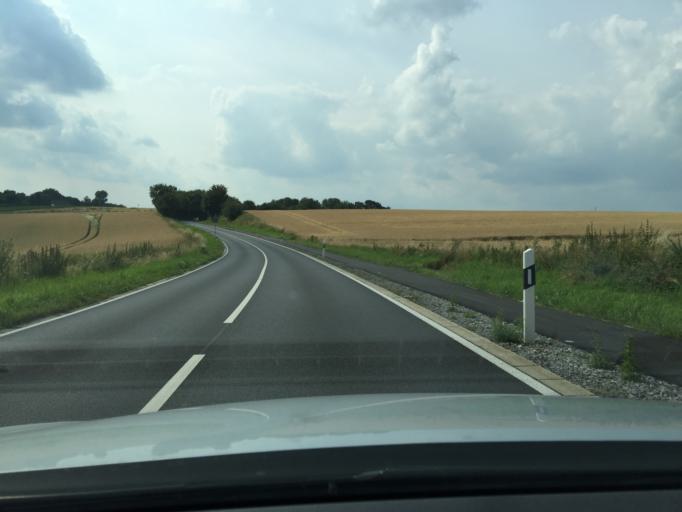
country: DE
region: North Rhine-Westphalia
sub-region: Regierungsbezirk Dusseldorf
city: Velbert
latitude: 51.3595
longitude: 7.0782
